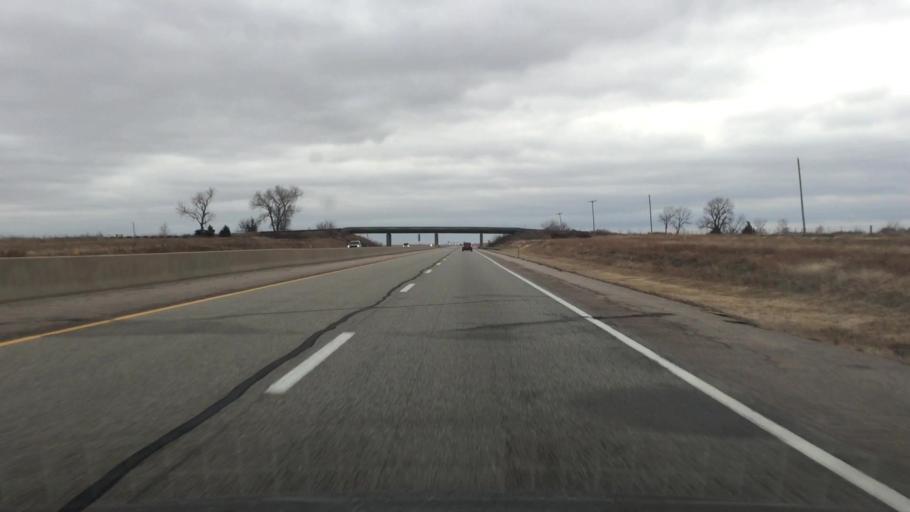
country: US
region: Kansas
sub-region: Butler County
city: El Dorado
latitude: 37.9137
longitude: -96.8046
